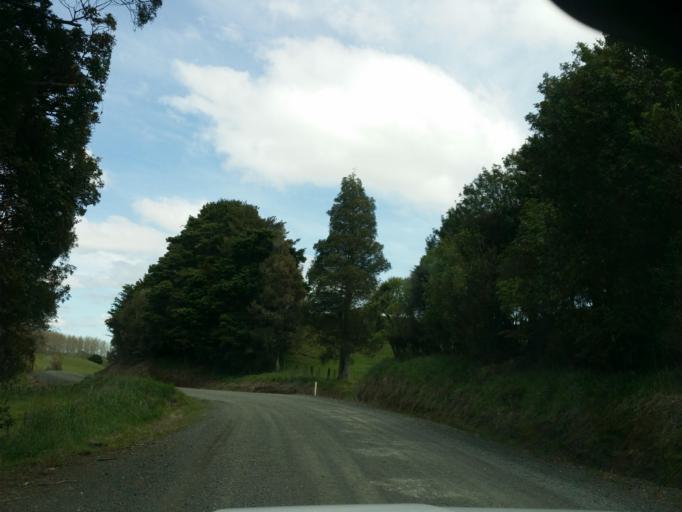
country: NZ
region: Northland
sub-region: Whangarei
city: Maungatapere
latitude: -35.9009
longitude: 174.1524
